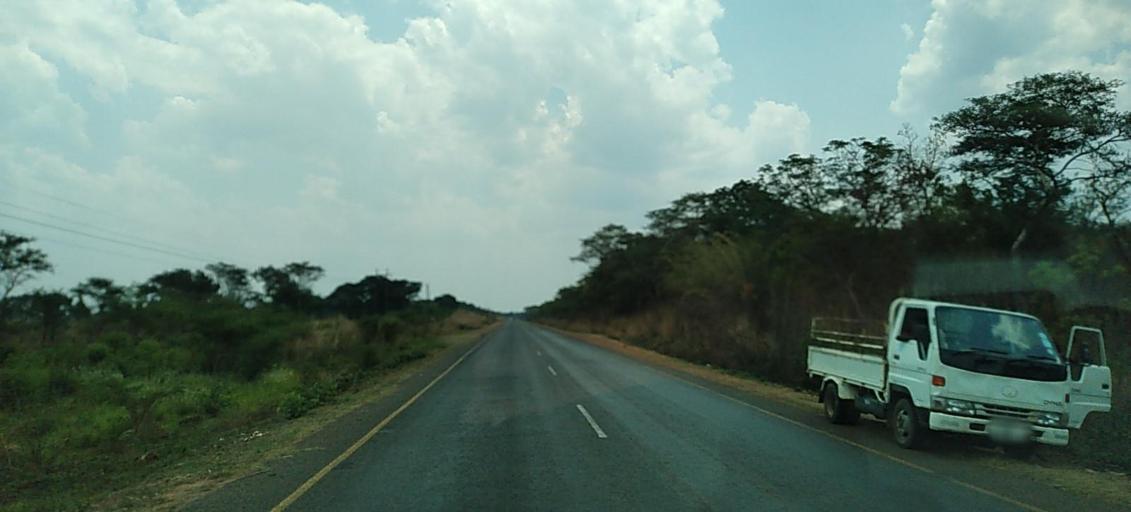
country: ZM
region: Copperbelt
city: Kalulushi
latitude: -12.8449
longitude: 28.0252
